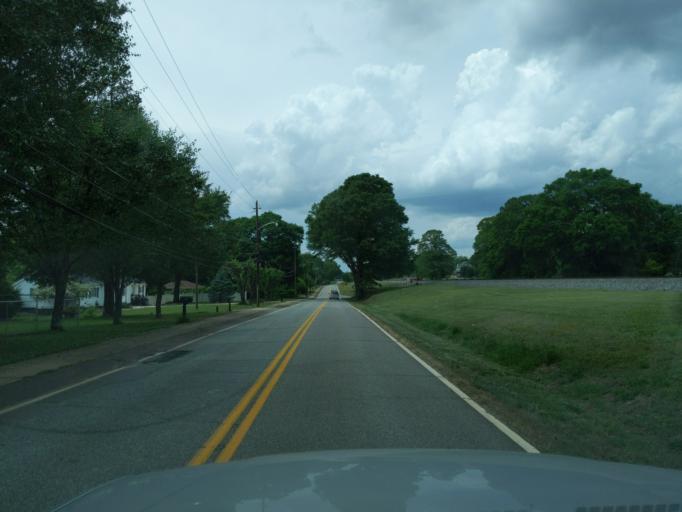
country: US
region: South Carolina
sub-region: Spartanburg County
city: Wellford
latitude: 34.9552
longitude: -82.0985
